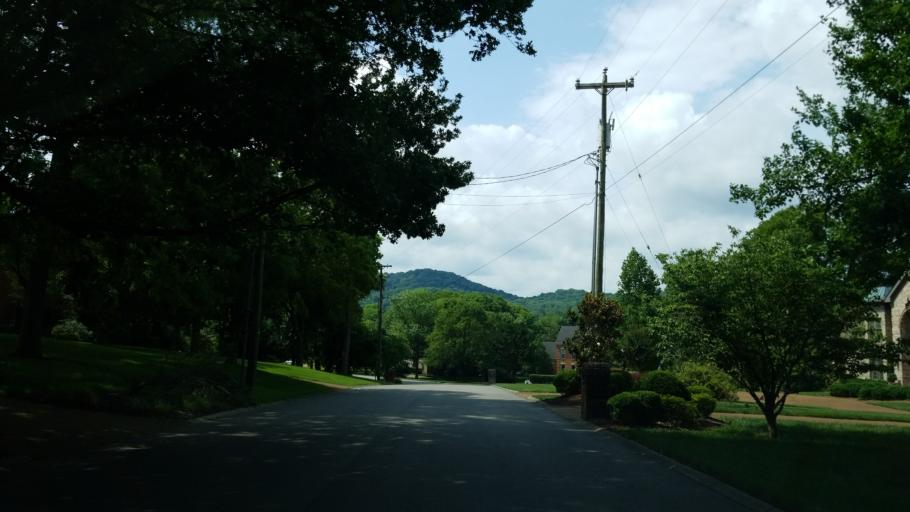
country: US
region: Tennessee
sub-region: Davidson County
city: Forest Hills
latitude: 36.0398
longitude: -86.8378
